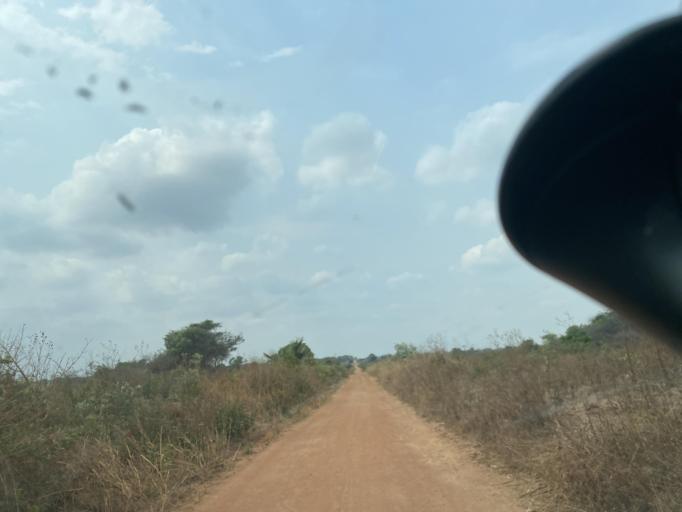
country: ZM
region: Lusaka
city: Lusaka
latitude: -15.1458
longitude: 28.3659
